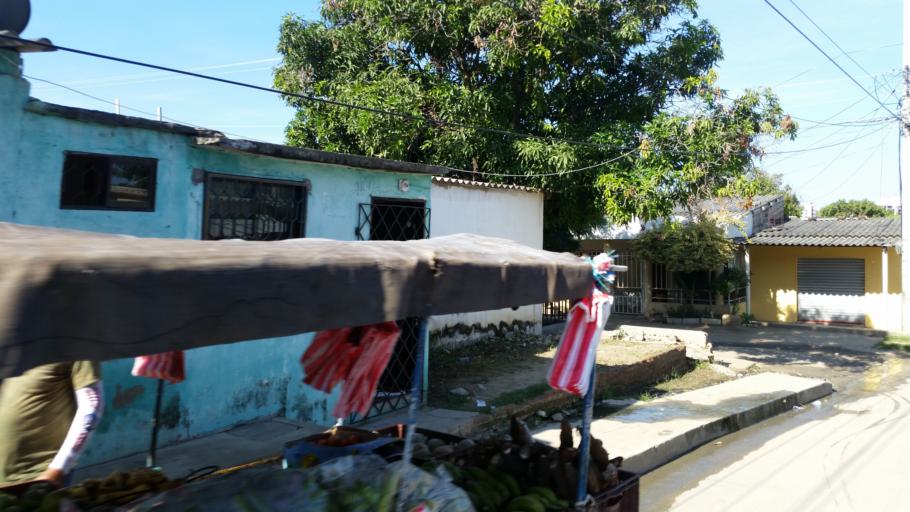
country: CO
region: Magdalena
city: Santa Marta
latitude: 11.1485
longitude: -74.2161
